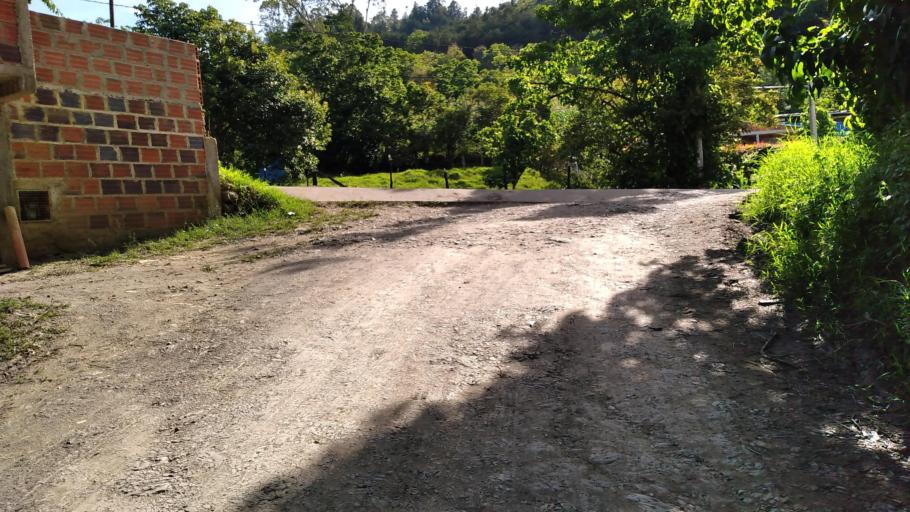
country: CO
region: Cundinamarca
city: Tenza
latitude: 5.0710
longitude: -73.4188
